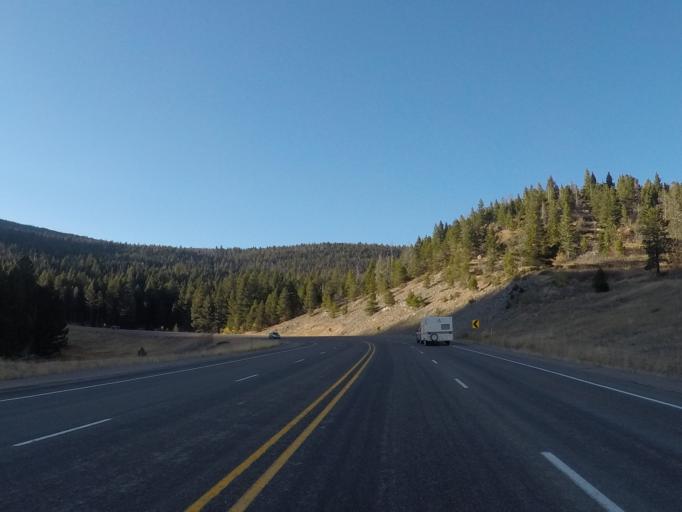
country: US
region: Montana
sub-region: Lewis and Clark County
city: Helena West Side
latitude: 46.5877
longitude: -112.2655
